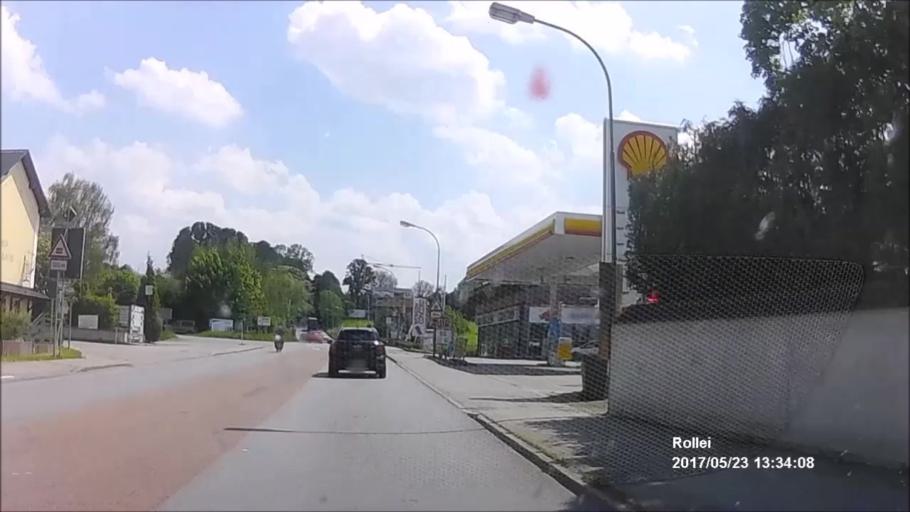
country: DE
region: Bavaria
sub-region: Upper Bavaria
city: Dorfen
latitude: 48.2678
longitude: 12.1551
